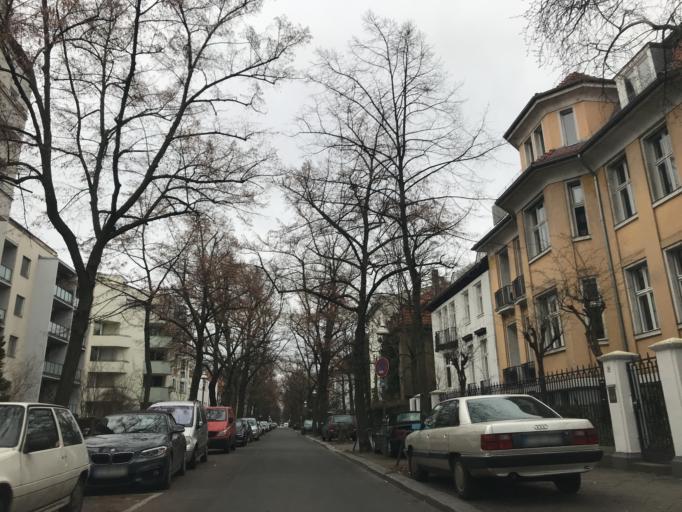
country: DE
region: Berlin
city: Westend
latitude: 52.5108
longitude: 13.2719
